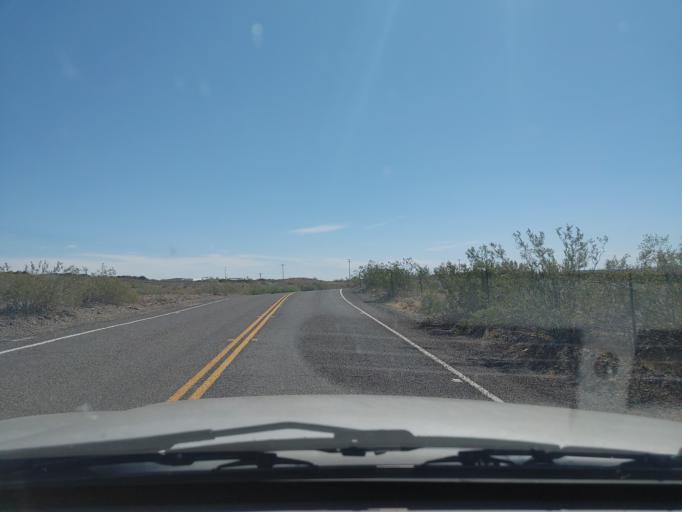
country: US
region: Arizona
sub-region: Maricopa County
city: Gila Bend
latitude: 32.9852
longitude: -113.3281
